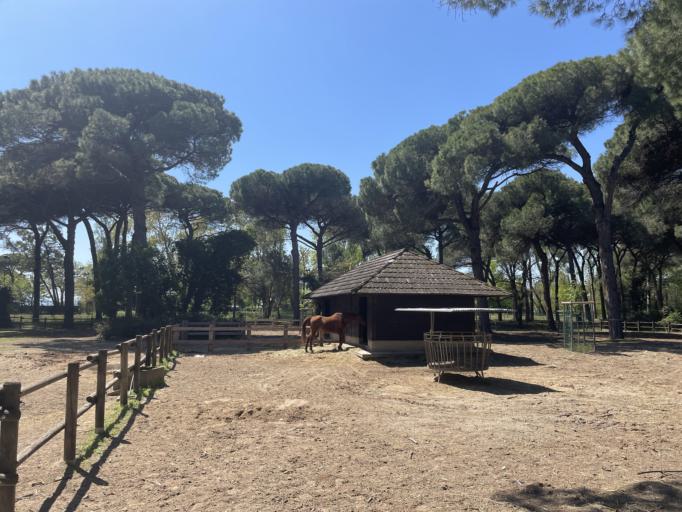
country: IT
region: Emilia-Romagna
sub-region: Provincia di Ravenna
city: Cervia
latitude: 44.2689
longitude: 12.3310
